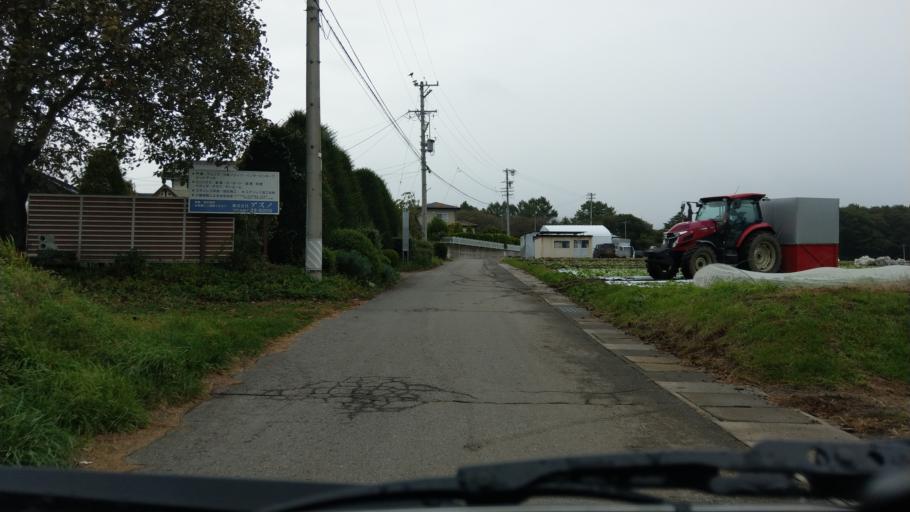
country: JP
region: Nagano
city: Komoro
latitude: 36.3381
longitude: 138.4549
